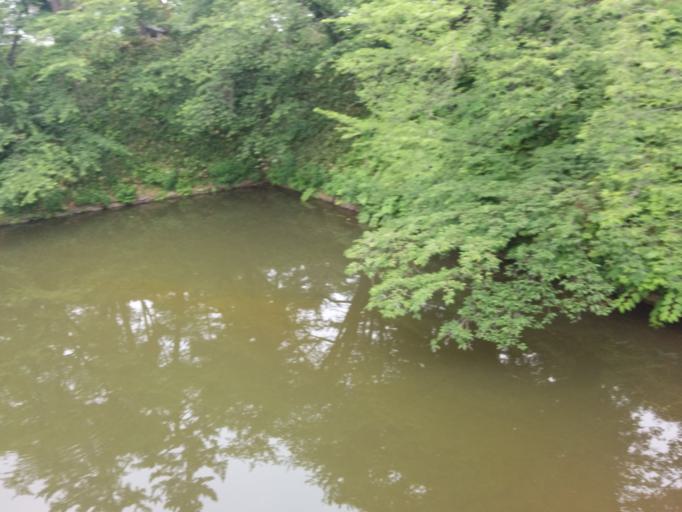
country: JP
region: Aomori
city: Hirosaki
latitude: 40.6059
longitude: 140.4636
